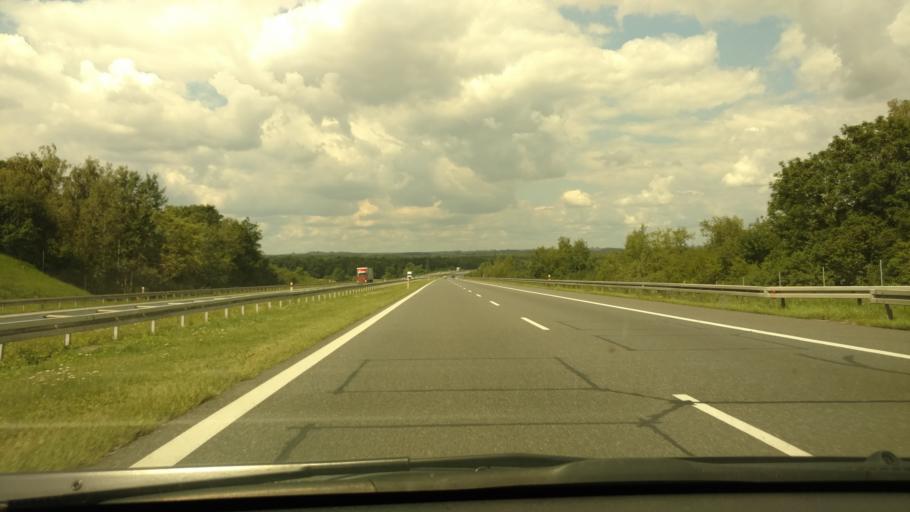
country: PL
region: Silesian Voivodeship
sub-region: Powiat bierunsko-ledzinski
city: Imielin
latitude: 50.1765
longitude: 19.2036
